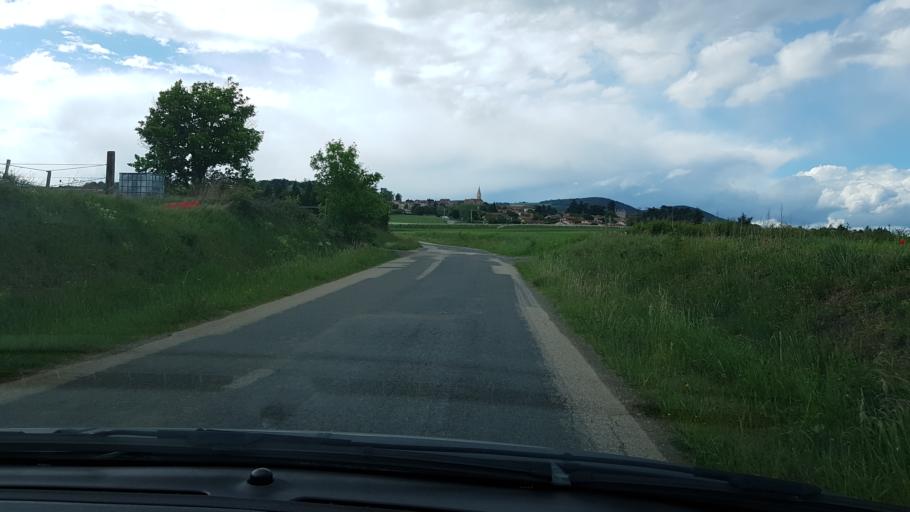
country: FR
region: Rhone-Alpes
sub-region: Departement du Rhone
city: Saint-Maurice-sur-Dargoire
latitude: 45.5760
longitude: 4.6403
